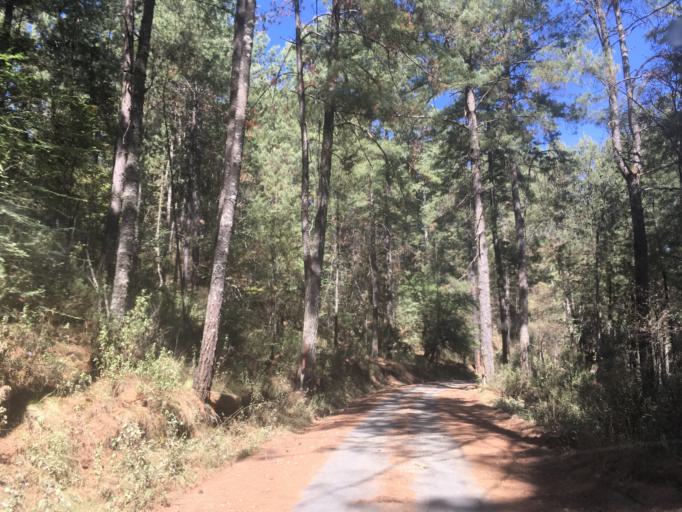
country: MX
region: Michoacan
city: Angahuan
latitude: 19.4909
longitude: -102.2060
